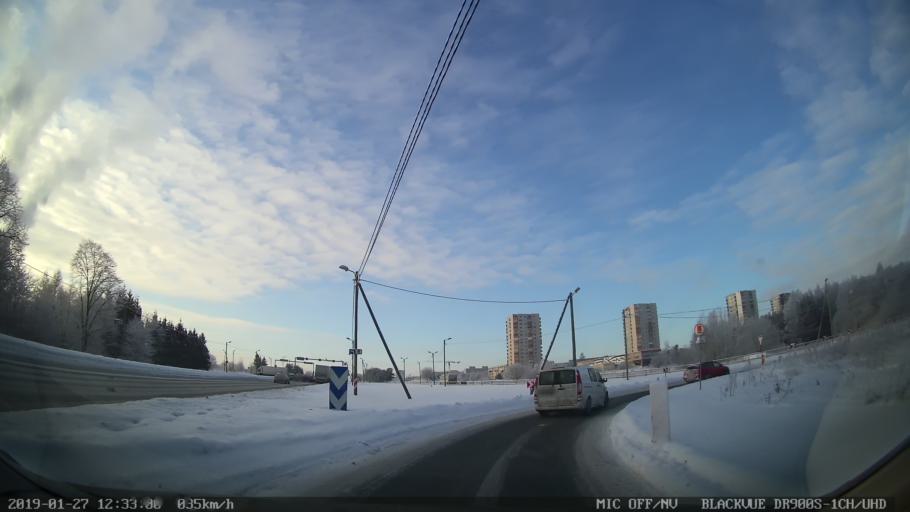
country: EE
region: Harju
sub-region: Tallinna linn
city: Kose
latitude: 59.4431
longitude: 24.9066
